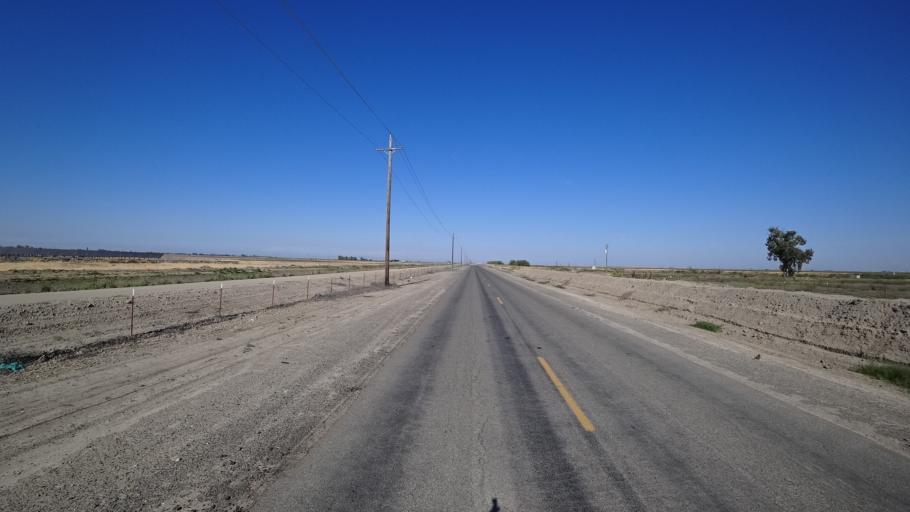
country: US
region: California
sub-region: Kings County
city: Corcoran
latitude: 36.1379
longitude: -119.5393
